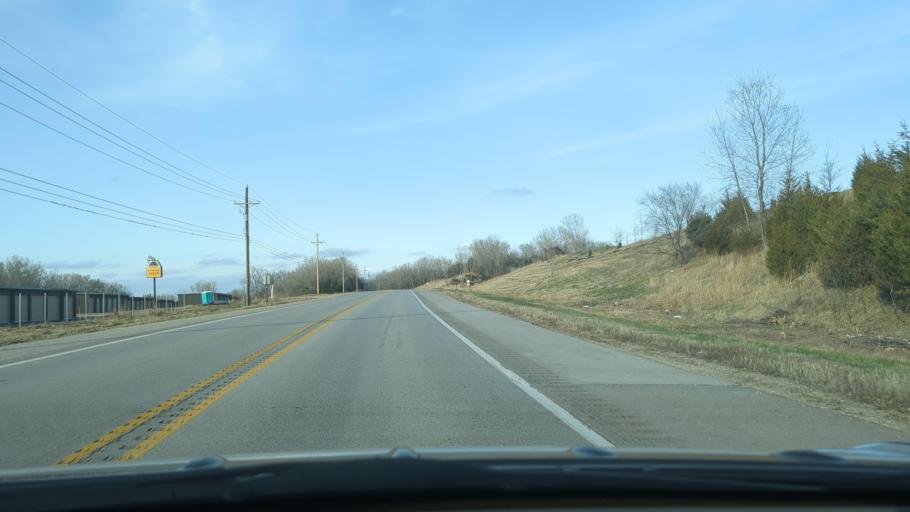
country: US
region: Nebraska
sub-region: Saunders County
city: Ashland
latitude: 41.0444
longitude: -96.3492
